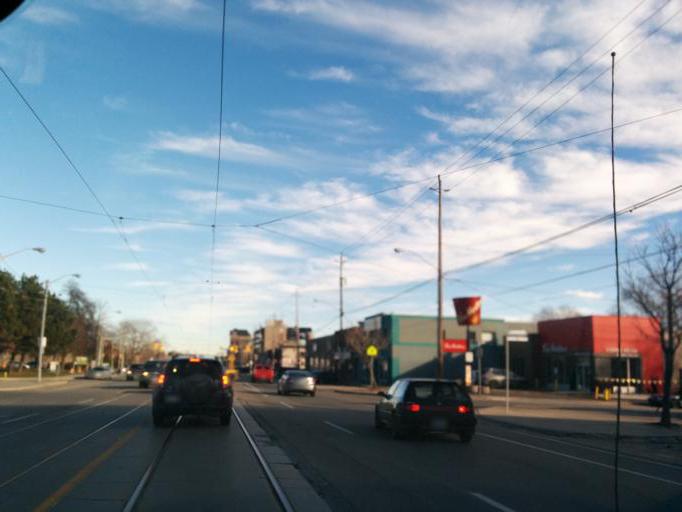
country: CA
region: Ontario
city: Etobicoke
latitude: 43.5931
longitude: -79.5397
